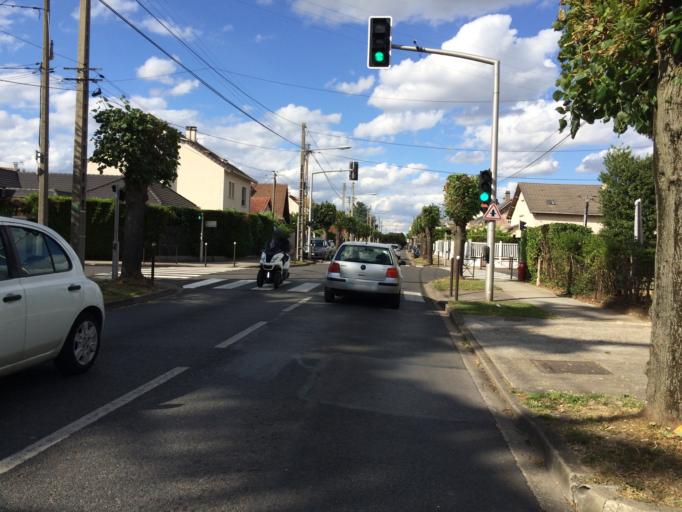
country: FR
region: Ile-de-France
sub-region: Departement de l'Essonne
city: Paray-Vieille-Poste
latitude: 48.7112
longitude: 2.3611
